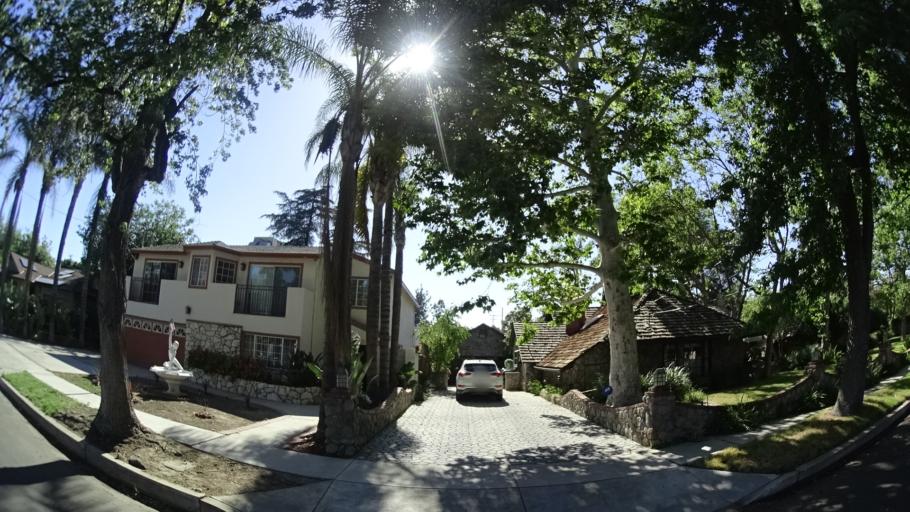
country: US
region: California
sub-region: Los Angeles County
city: North Hollywood
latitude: 34.1659
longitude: -118.4121
